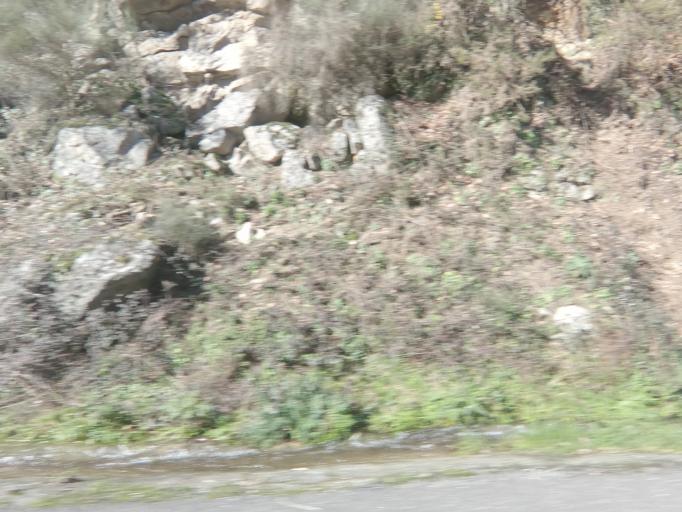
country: ES
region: Galicia
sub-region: Provincia de Ourense
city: Pinor
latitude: 42.5172
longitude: -8.0148
